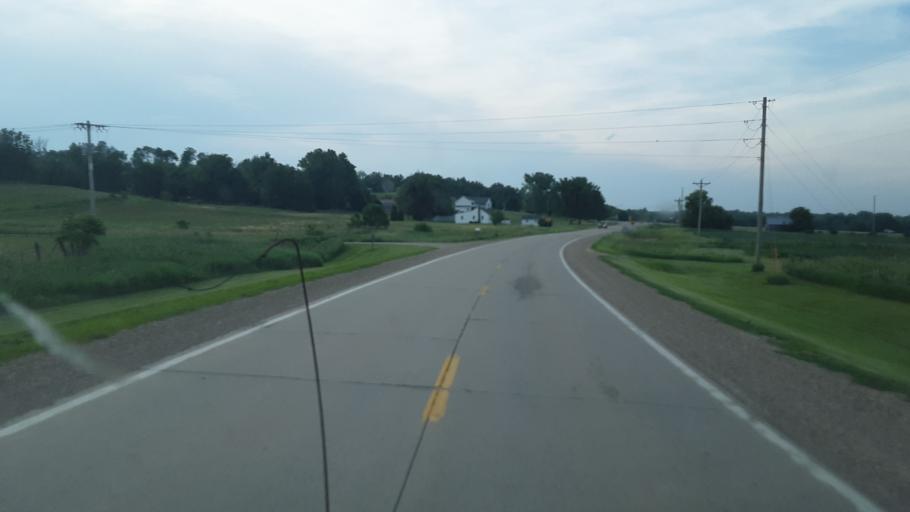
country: US
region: Iowa
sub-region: Tama County
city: Toledo
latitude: 42.0011
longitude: -92.7295
